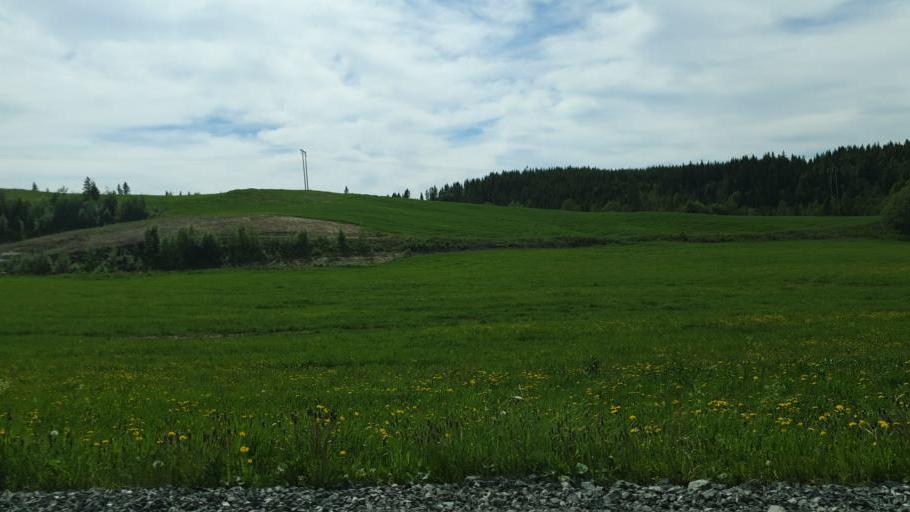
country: NO
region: Nord-Trondelag
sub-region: Leksvik
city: Leksvik
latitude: 63.6867
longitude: 10.5543
